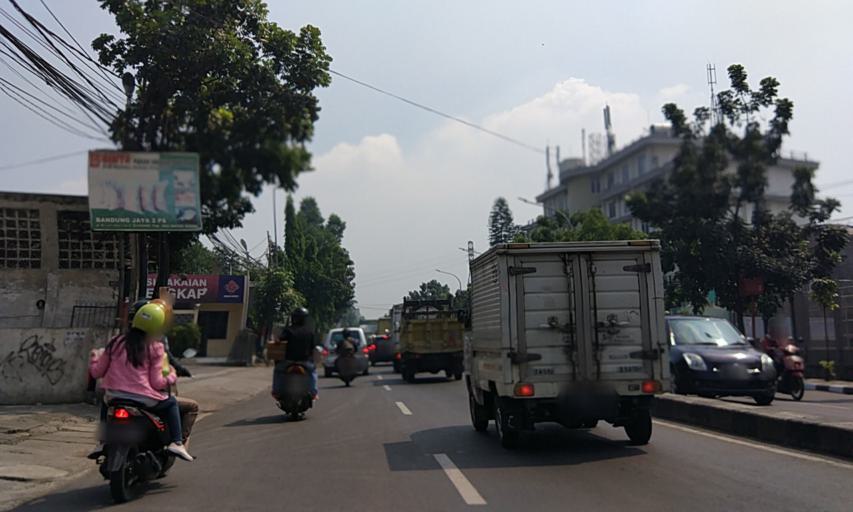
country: ID
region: West Java
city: Cimahi
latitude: -6.9094
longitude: 107.5683
